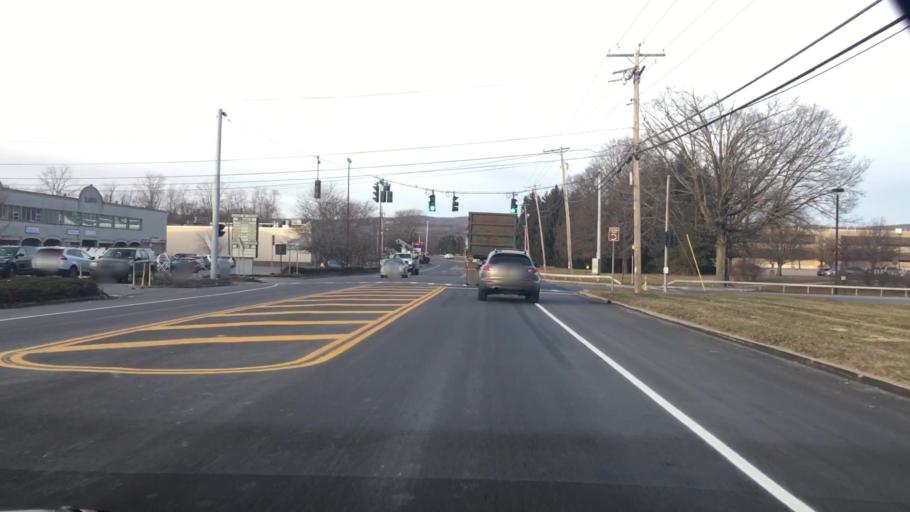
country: US
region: New York
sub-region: Dutchess County
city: Crown Heights
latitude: 41.6511
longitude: -73.9318
